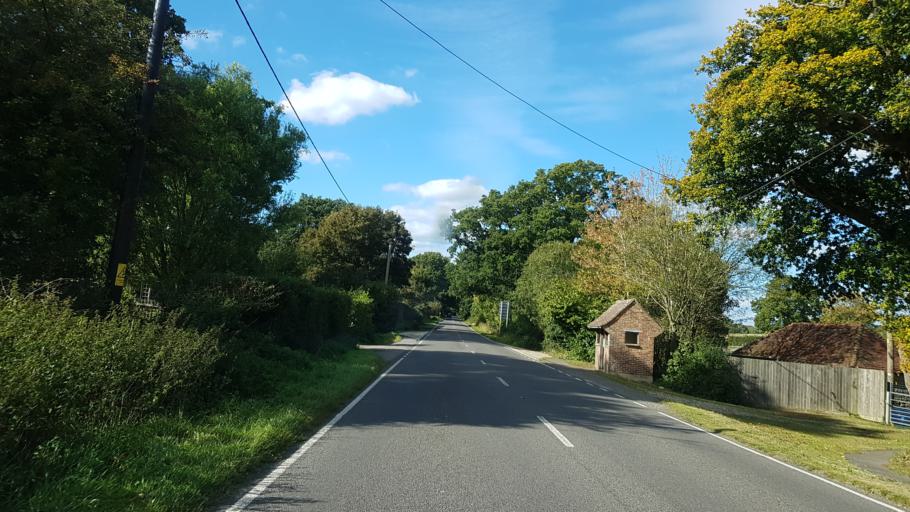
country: GB
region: England
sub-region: West Sussex
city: Petworth
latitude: 50.9959
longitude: -0.6131
